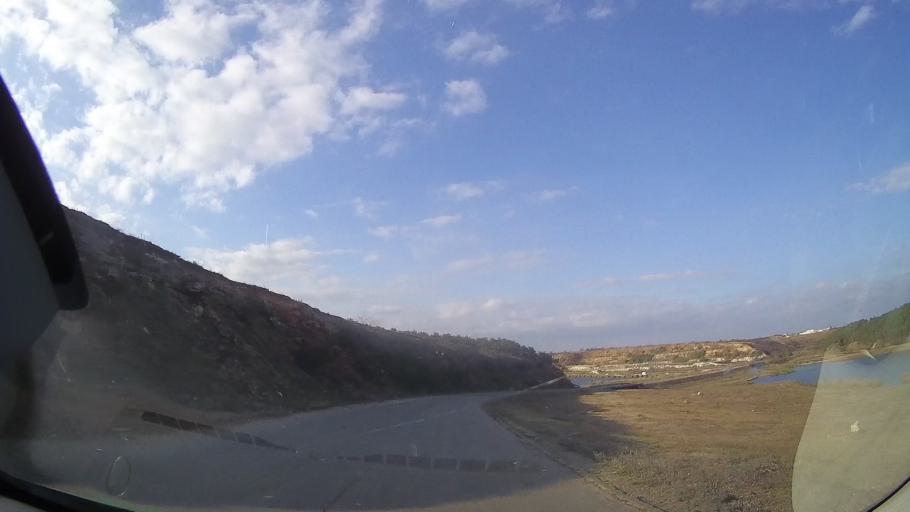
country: RO
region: Constanta
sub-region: Comuna Limanu
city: Limanu
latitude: 43.8105
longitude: 28.5180
